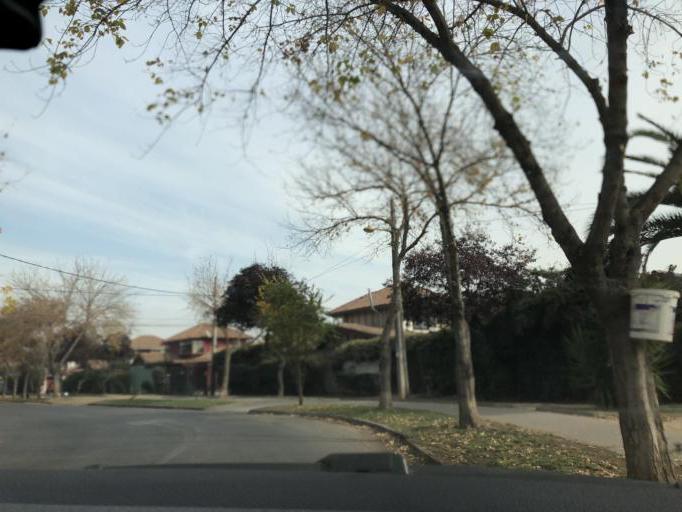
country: CL
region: Santiago Metropolitan
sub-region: Provincia de Cordillera
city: Puente Alto
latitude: -33.5491
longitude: -70.5643
